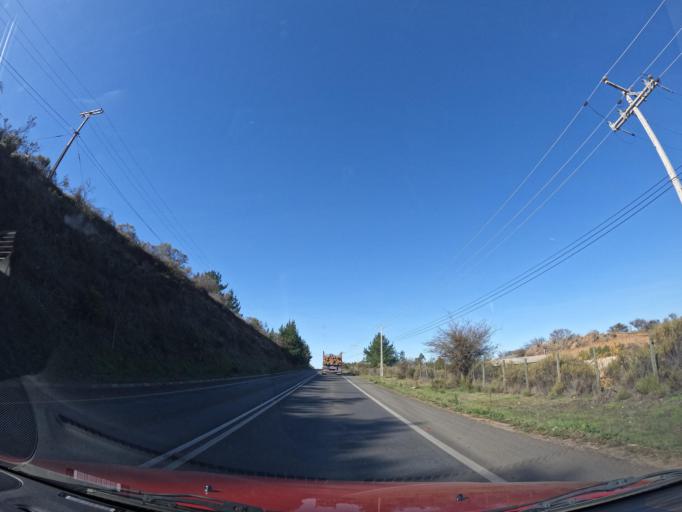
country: CL
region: Maule
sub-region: Provincia de Cauquenes
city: Cauquenes
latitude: -35.9609
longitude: -72.2556
